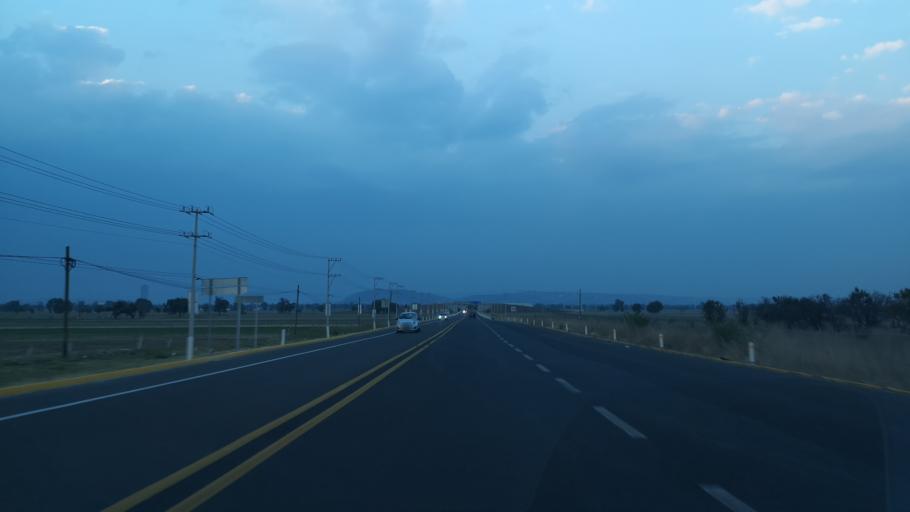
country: MX
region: Puebla
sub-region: Huejotzingo
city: Los Encinos
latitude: 19.1809
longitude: -98.3724
